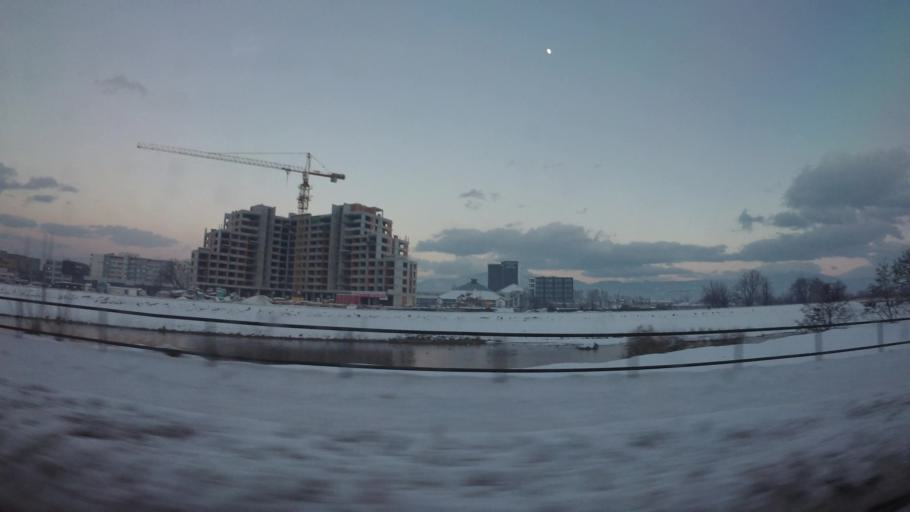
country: BA
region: Federation of Bosnia and Herzegovina
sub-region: Kanton Sarajevo
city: Sarajevo
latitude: 43.8270
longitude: 18.3085
